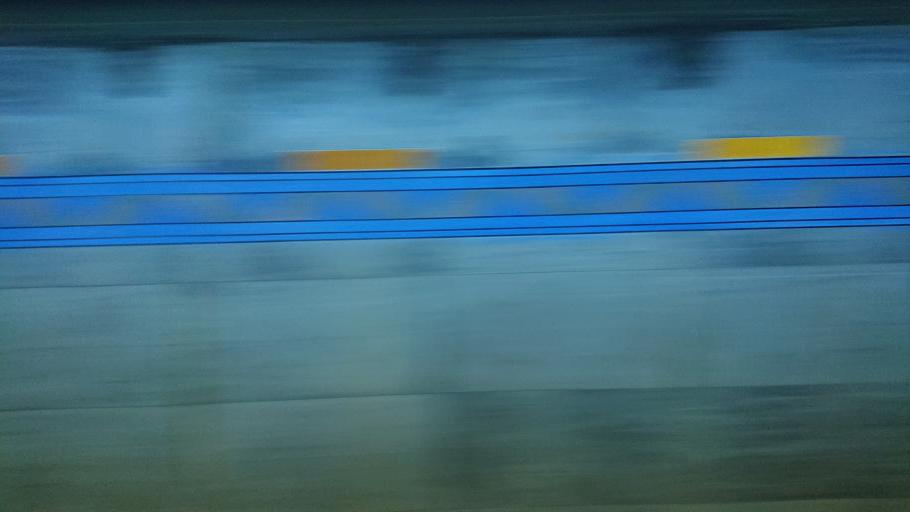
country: TW
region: Taiwan
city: Lugu
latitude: 23.4741
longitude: 120.8378
